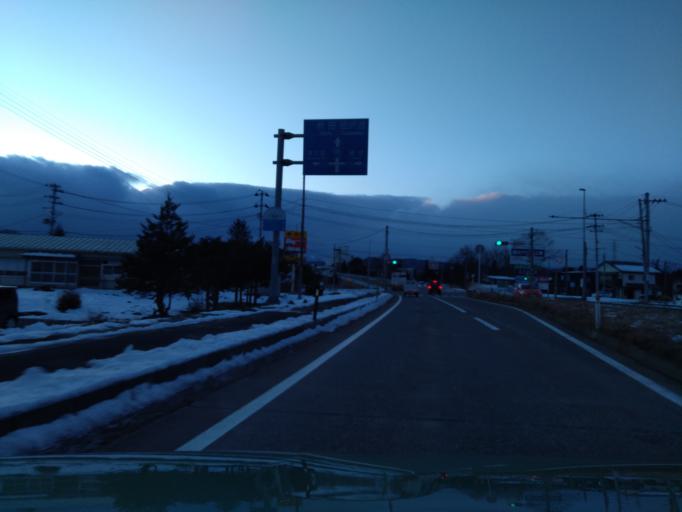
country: JP
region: Iwate
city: Shizukuishi
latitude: 39.7029
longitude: 140.9707
